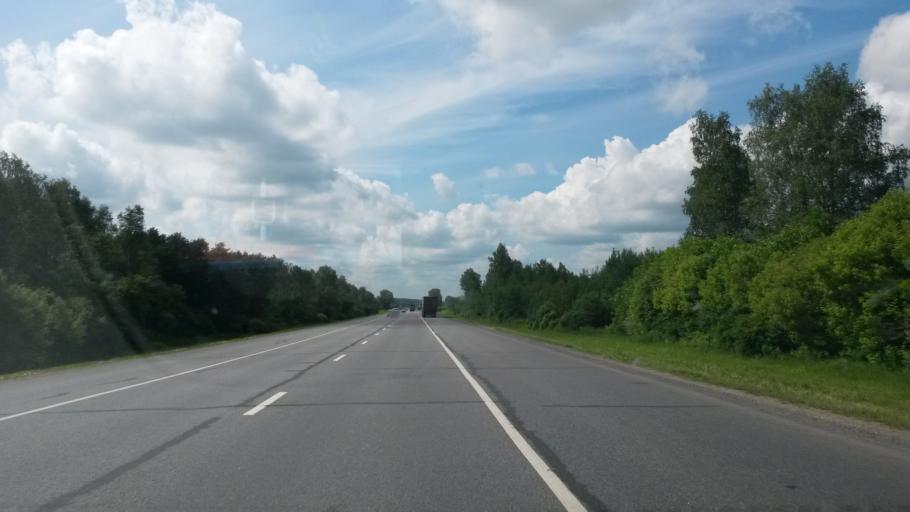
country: RU
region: Jaroslavl
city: Petrovsk
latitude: 57.0606
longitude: 39.3030
